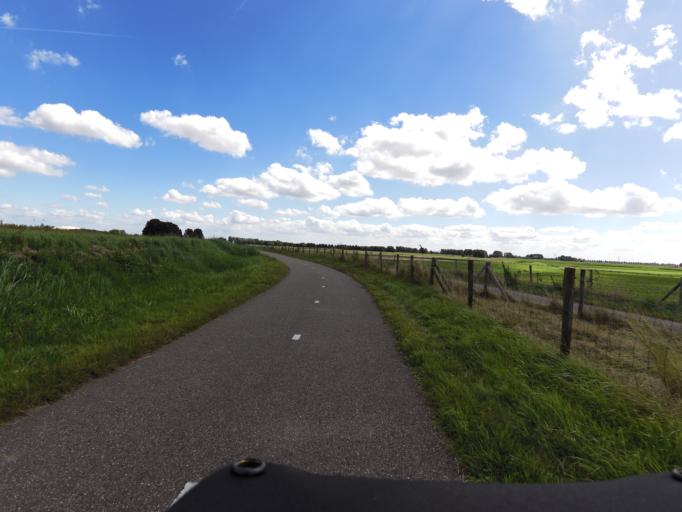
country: NL
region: South Holland
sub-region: Gemeente Oud-Beijerland
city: Oud-Beijerland
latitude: 51.8355
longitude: 4.3802
